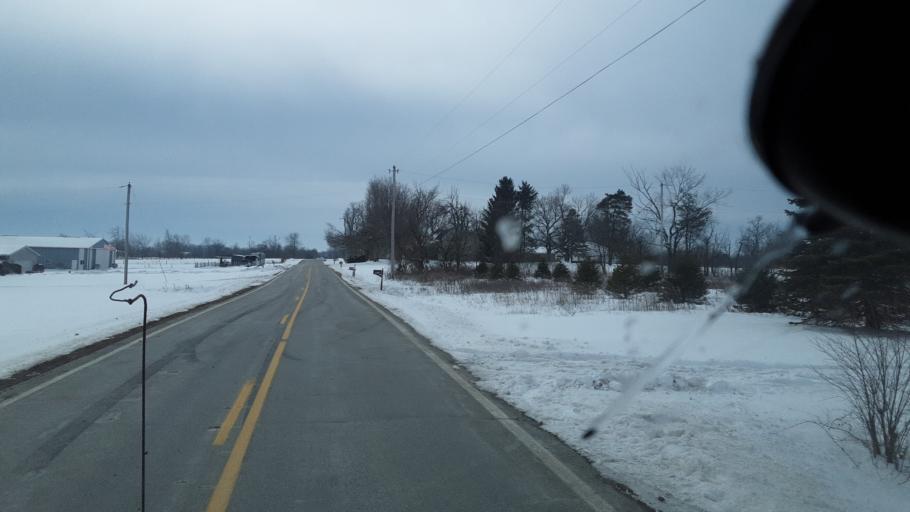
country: US
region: Ohio
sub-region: Madison County
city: Choctaw Lake
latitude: 39.9709
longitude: -83.5018
